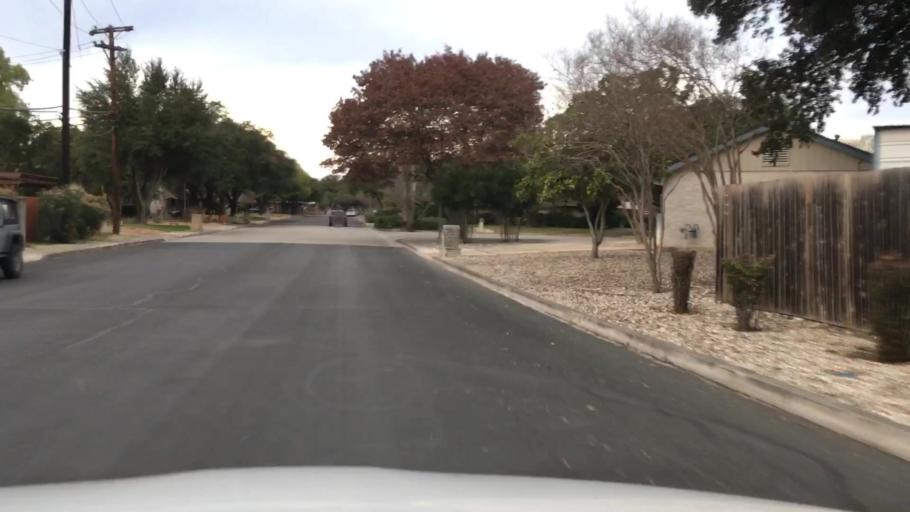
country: US
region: Texas
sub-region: Bexar County
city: Windcrest
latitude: 29.5139
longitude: -98.3843
